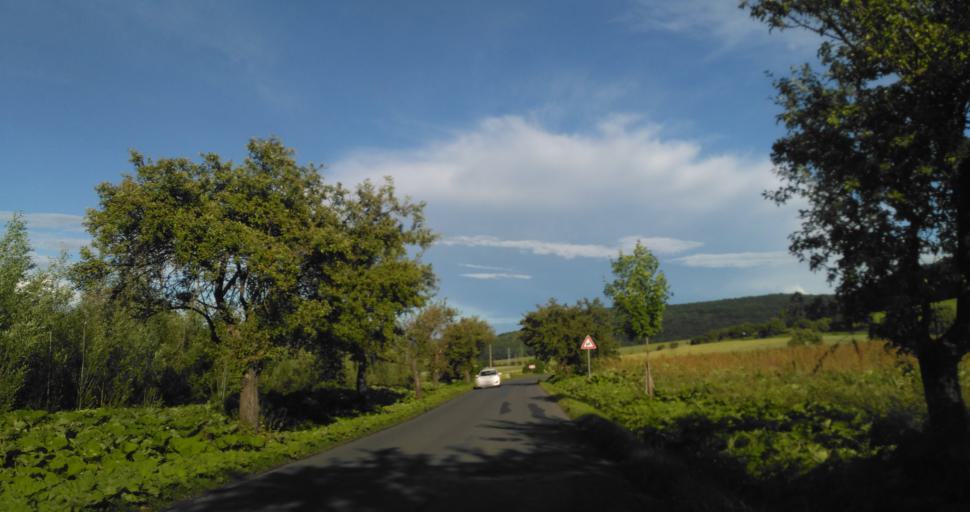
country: CZ
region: Central Bohemia
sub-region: Okres Beroun
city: Beroun
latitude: 49.9102
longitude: 14.0988
